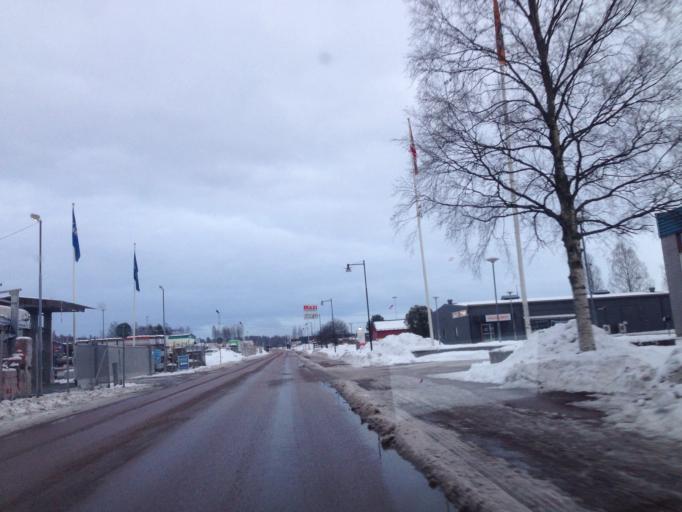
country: SE
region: Dalarna
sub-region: Mora Kommun
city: Mora
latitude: 61.0079
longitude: 14.5918
